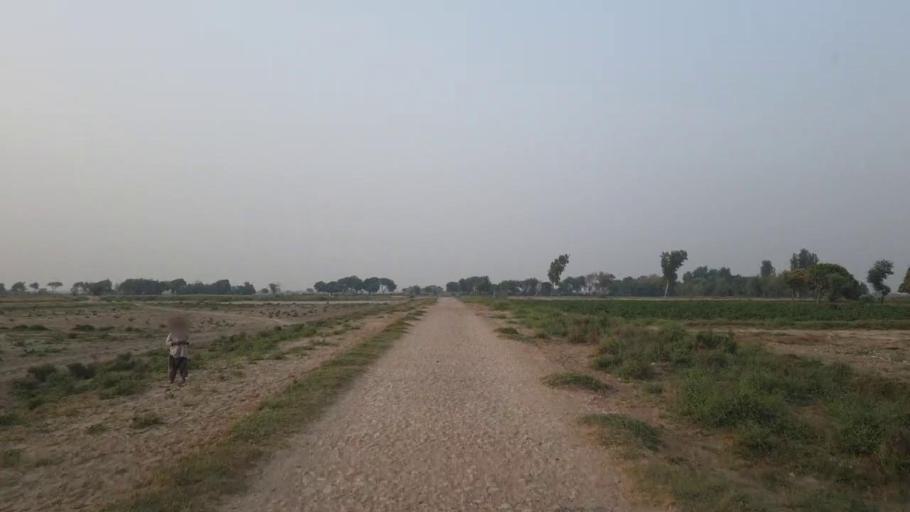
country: PK
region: Sindh
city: Mirpur Batoro
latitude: 24.6614
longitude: 68.3845
